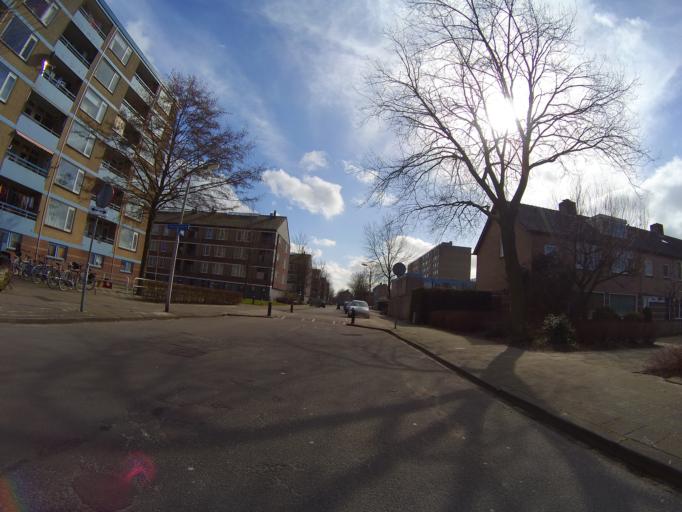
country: NL
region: Utrecht
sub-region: Gemeente Amersfoort
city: Randenbroek
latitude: 52.1578
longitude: 5.4139
